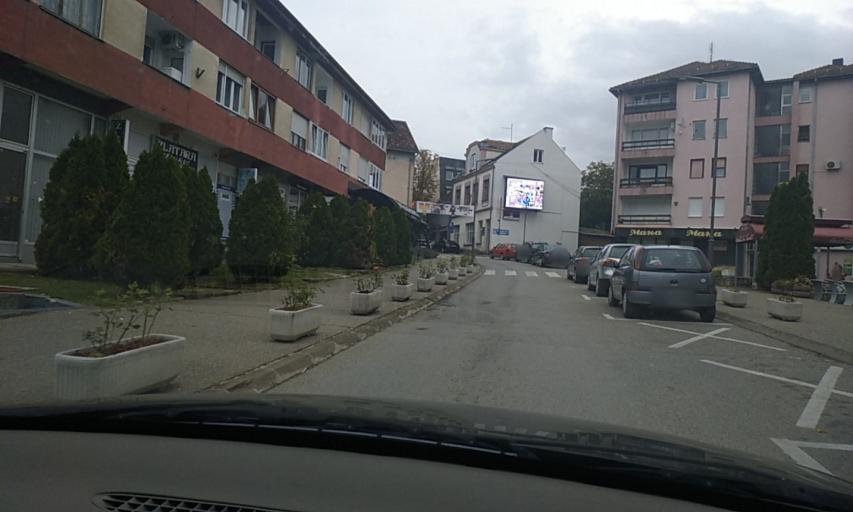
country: BA
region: Republika Srpska
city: Prnjavor
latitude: 44.8685
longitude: 17.6628
